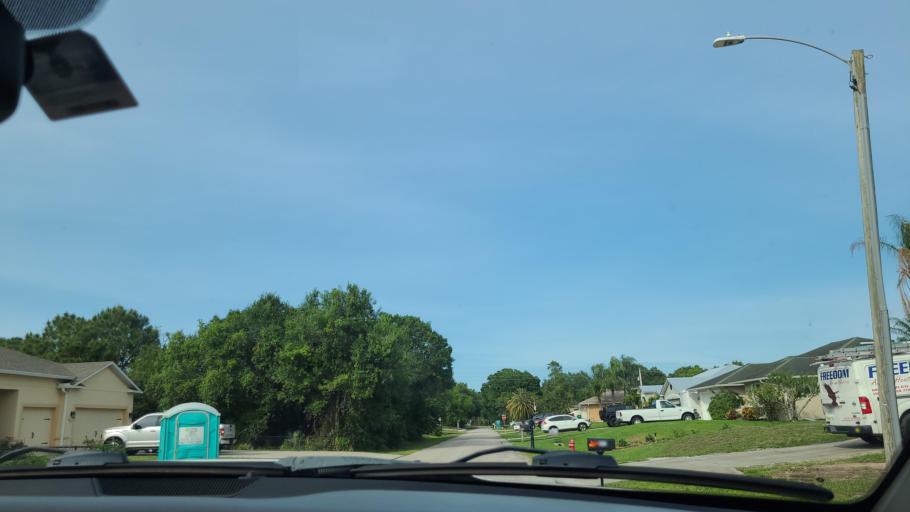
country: US
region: Florida
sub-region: Indian River County
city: Sebastian
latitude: 27.7864
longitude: -80.4892
